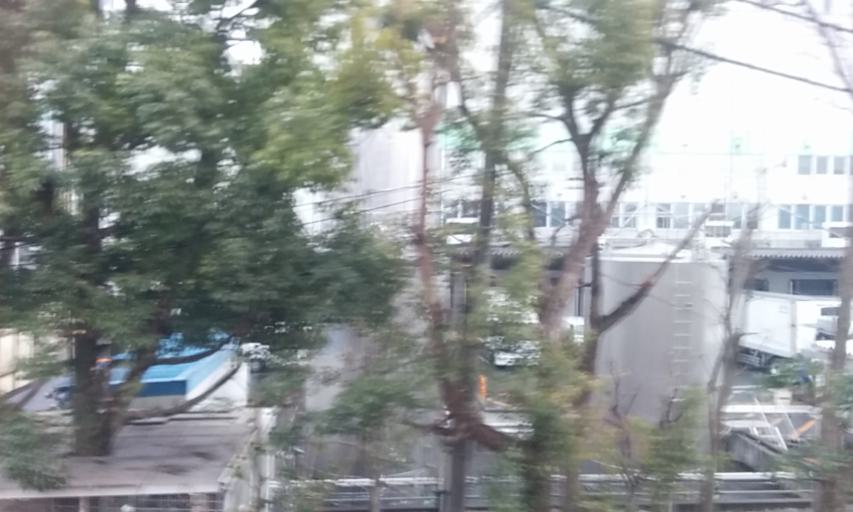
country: JP
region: Tokyo
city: Kokubunji
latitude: 35.6577
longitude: 139.4517
